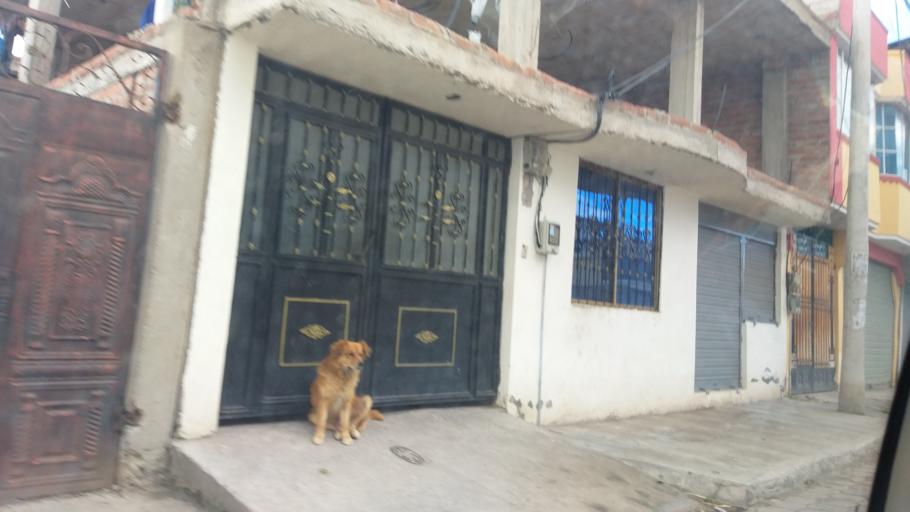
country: EC
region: Chimborazo
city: Riobamba
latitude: -1.6875
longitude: -78.6304
